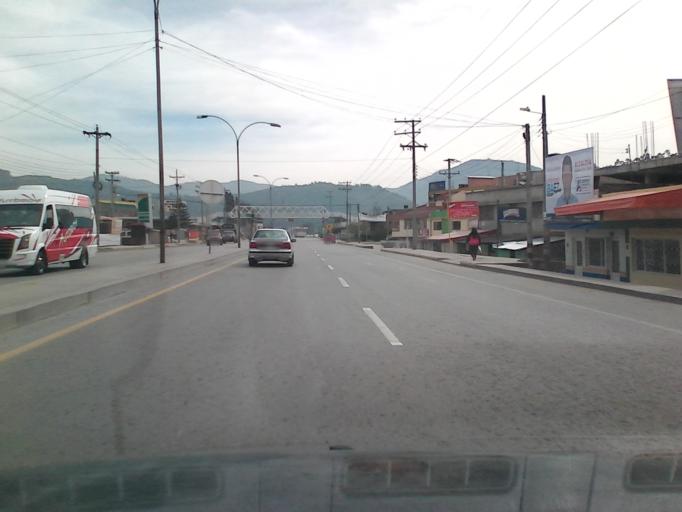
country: CO
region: Boyaca
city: Duitama
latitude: 5.8088
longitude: -73.0197
